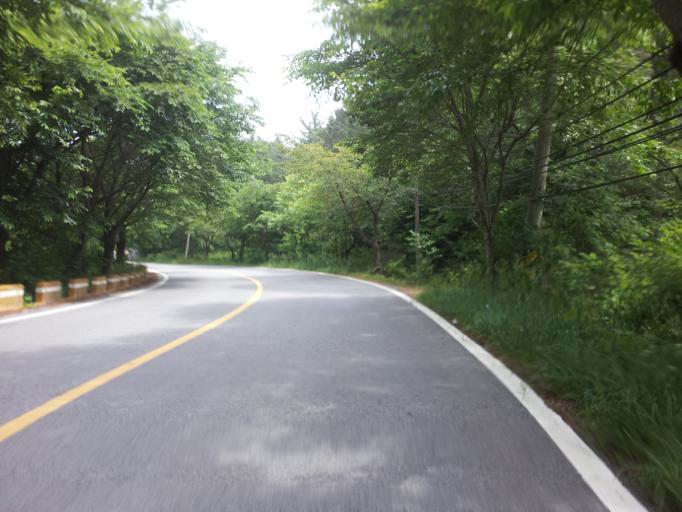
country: KR
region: Chungcheongbuk-do
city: Okcheon
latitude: 36.3847
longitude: 127.5189
